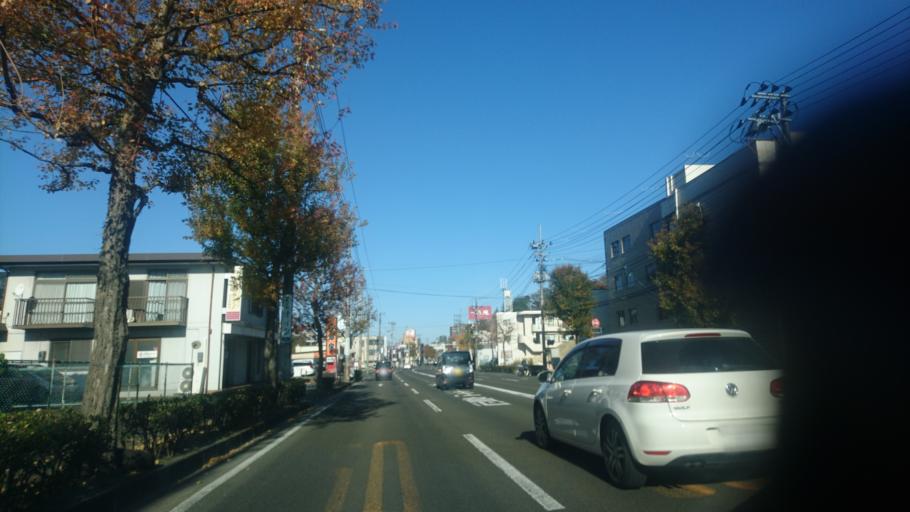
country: JP
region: Miyagi
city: Sendai-shi
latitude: 38.2955
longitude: 140.8738
